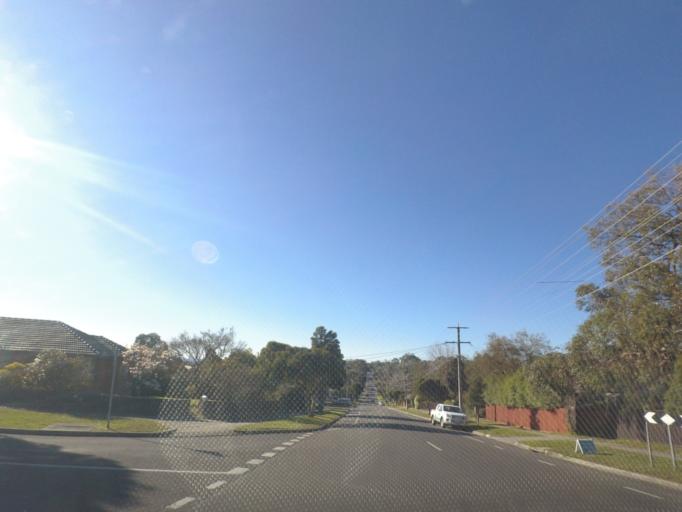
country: AU
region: Victoria
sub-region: Yarra Ranges
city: Kilsyth
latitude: -37.7972
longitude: 145.3133
